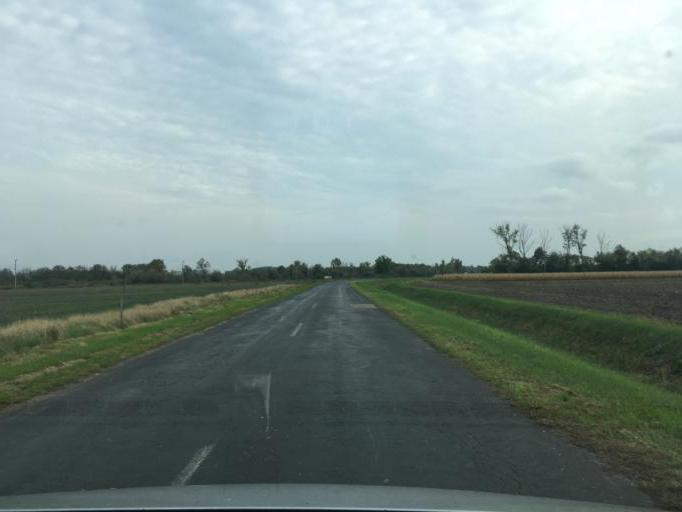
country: HU
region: Gyor-Moson-Sopron
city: Fertod
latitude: 47.6520
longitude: 16.8593
